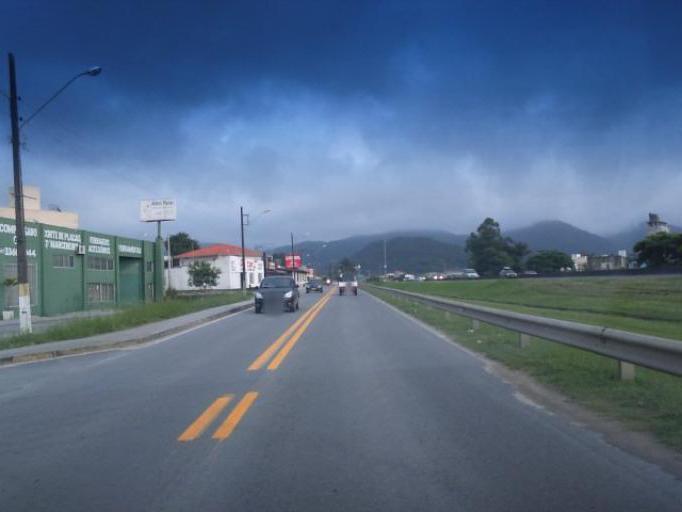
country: BR
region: Santa Catarina
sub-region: Itapema
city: Itapema
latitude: -27.1043
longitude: -48.6166
